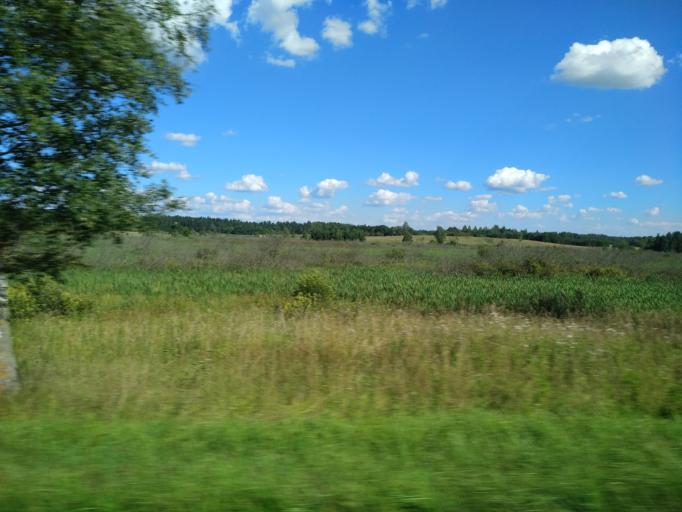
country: BY
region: Vitebsk
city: Mosar
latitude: 55.1139
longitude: 27.2059
